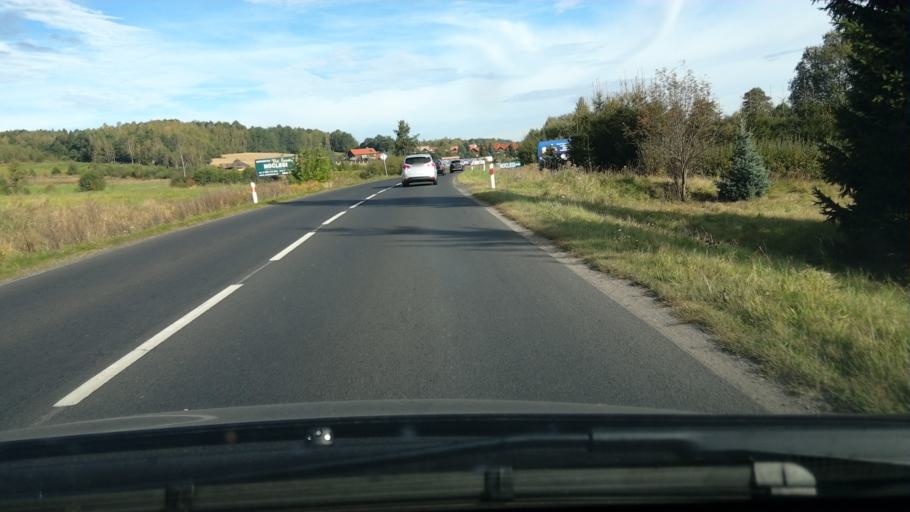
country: PL
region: Lower Silesian Voivodeship
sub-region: Powiat jeleniogorski
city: Myslakowice
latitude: 50.8461
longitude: 15.7735
